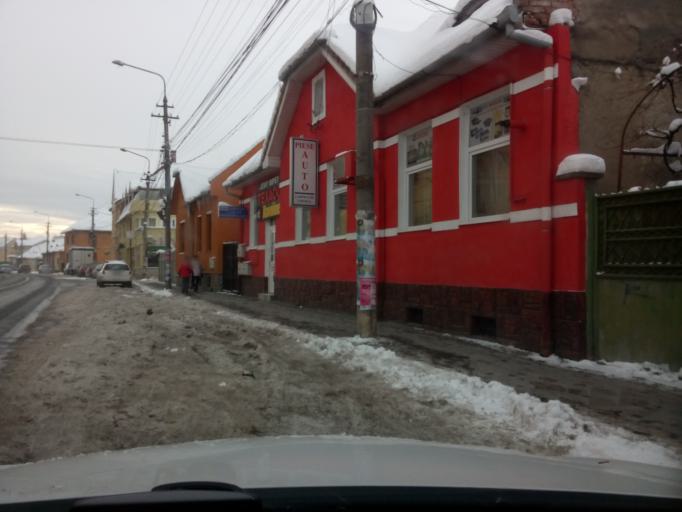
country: RO
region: Sibiu
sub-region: Municipiul Sibiu
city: Sibiu
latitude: 45.8060
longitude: 24.1449
